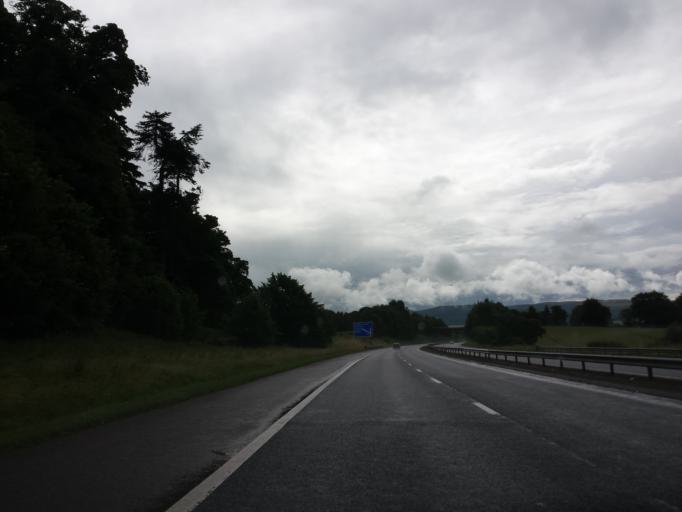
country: GB
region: Scotland
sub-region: Perth and Kinross
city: Bridge of Earn
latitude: 56.3613
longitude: -3.4113
